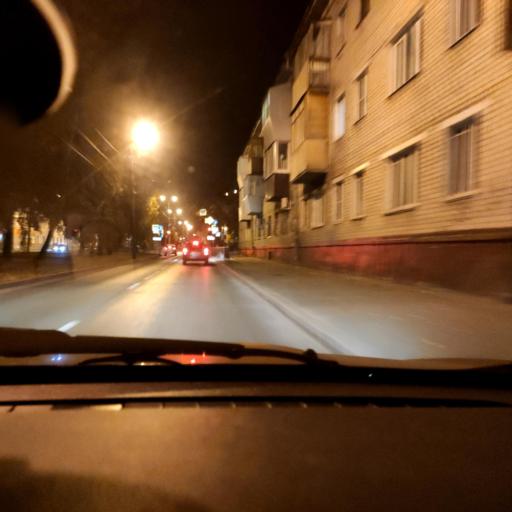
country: RU
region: Samara
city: Tol'yatti
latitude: 53.5166
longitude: 49.4066
